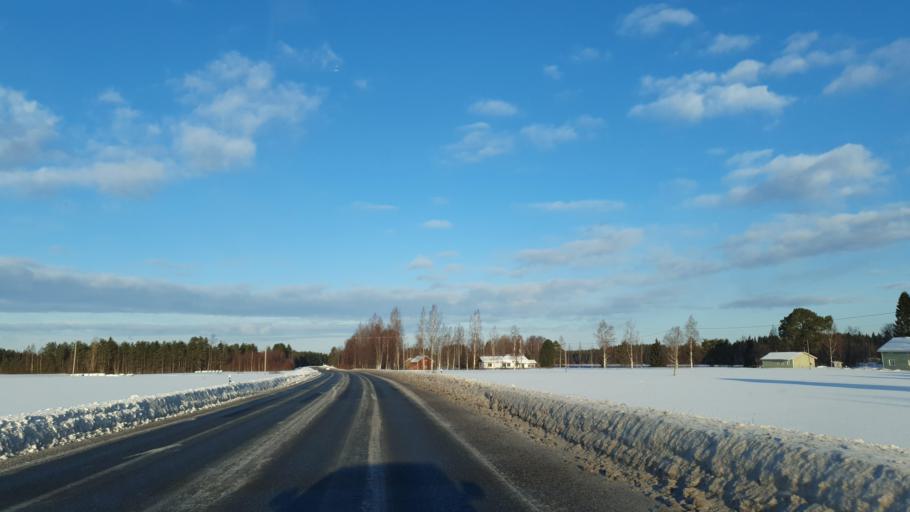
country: FI
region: Northern Ostrobothnia
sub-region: Oulunkaari
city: Utajaervi
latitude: 64.7233
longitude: 26.5021
